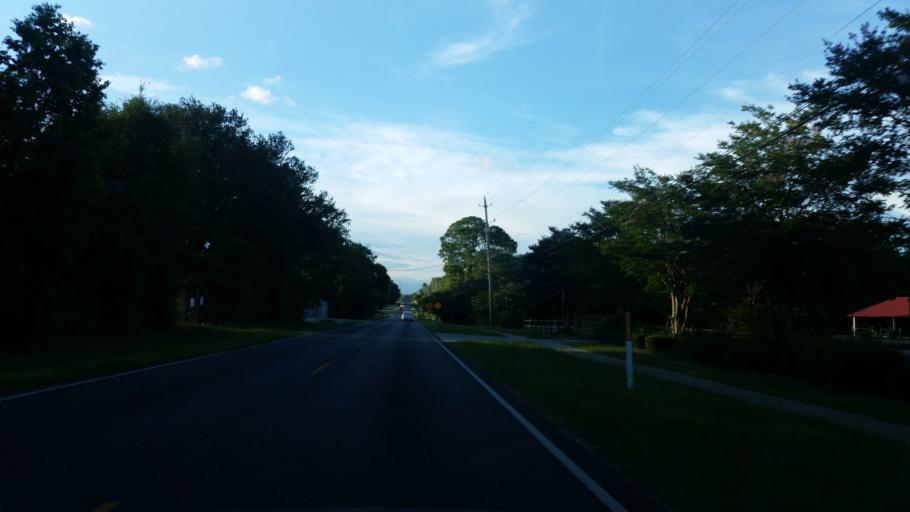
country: US
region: Florida
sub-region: Escambia County
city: Warrington
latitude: 30.3975
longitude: -87.2735
